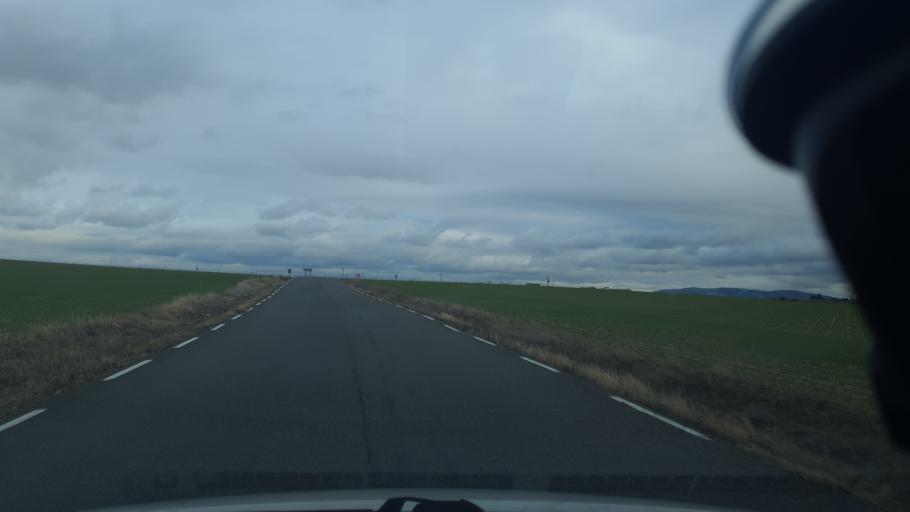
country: ES
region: Castille and Leon
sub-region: Provincia de Avila
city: Velayos
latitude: 40.8334
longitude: -4.6115
